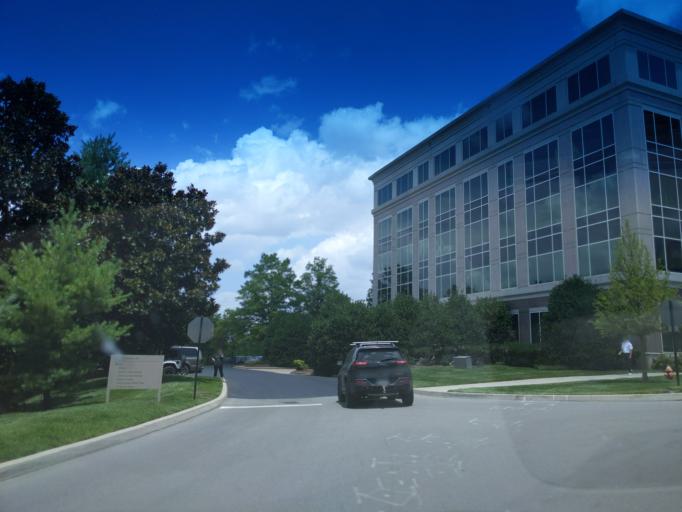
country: US
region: Tennessee
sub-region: Williamson County
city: Brentwood
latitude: 36.0422
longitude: -86.7708
